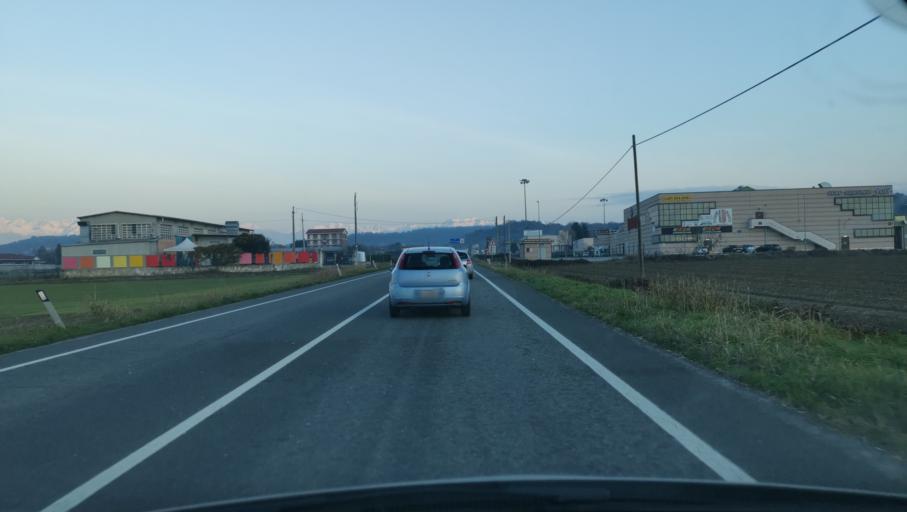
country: IT
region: Piedmont
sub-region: Provincia di Torino
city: Caluso
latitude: 45.3043
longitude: 7.8787
